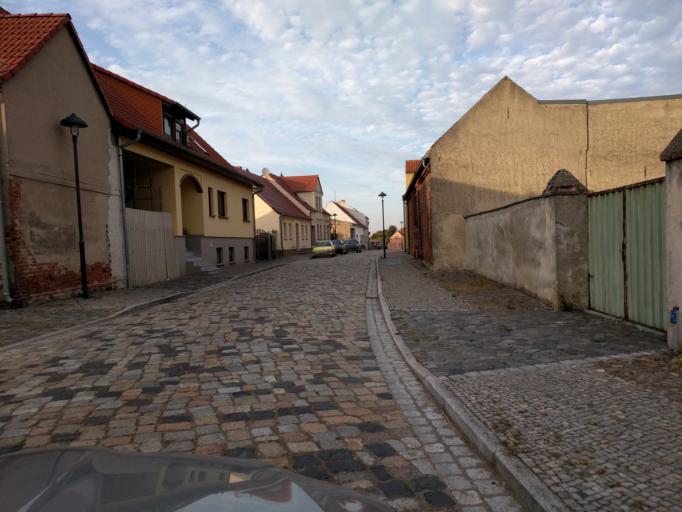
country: DE
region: Brandenburg
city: Ziesar
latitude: 52.2611
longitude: 12.2898
